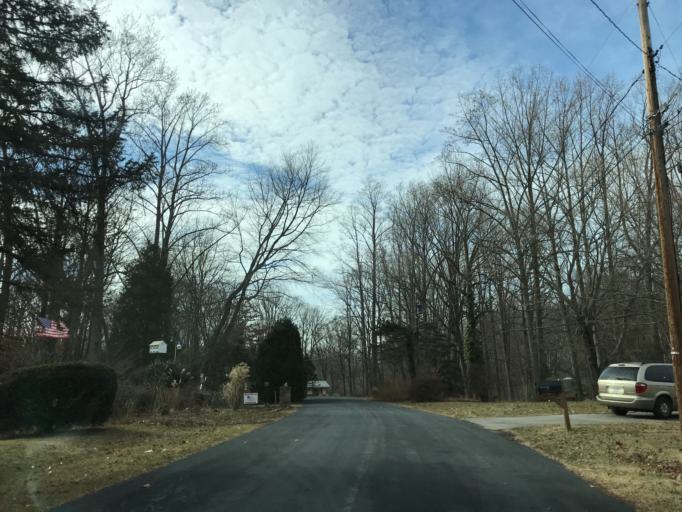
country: US
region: Maryland
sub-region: Harford County
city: Joppatowne
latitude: 39.4469
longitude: -76.3764
